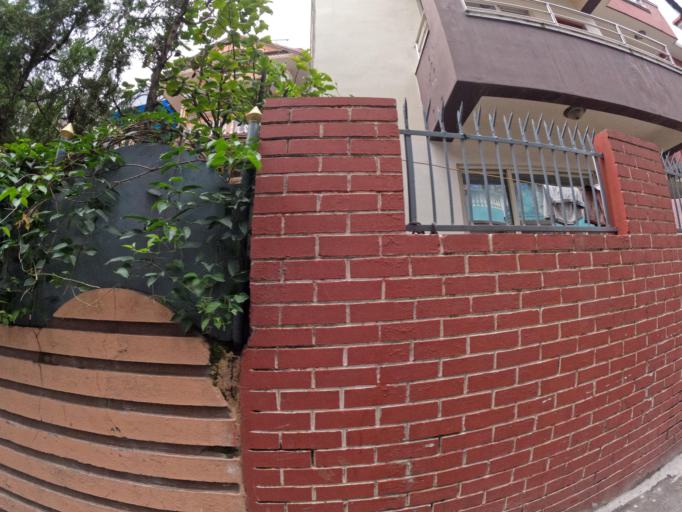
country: NP
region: Central Region
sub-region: Bagmati Zone
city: Kathmandu
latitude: 27.7371
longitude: 85.3157
